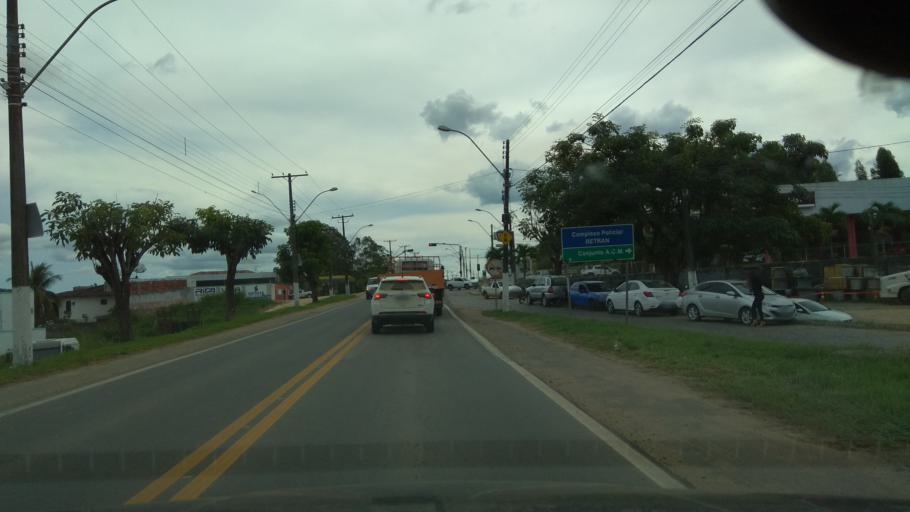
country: BR
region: Bahia
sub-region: Ipiau
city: Ipiau
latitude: -14.1412
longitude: -39.7261
